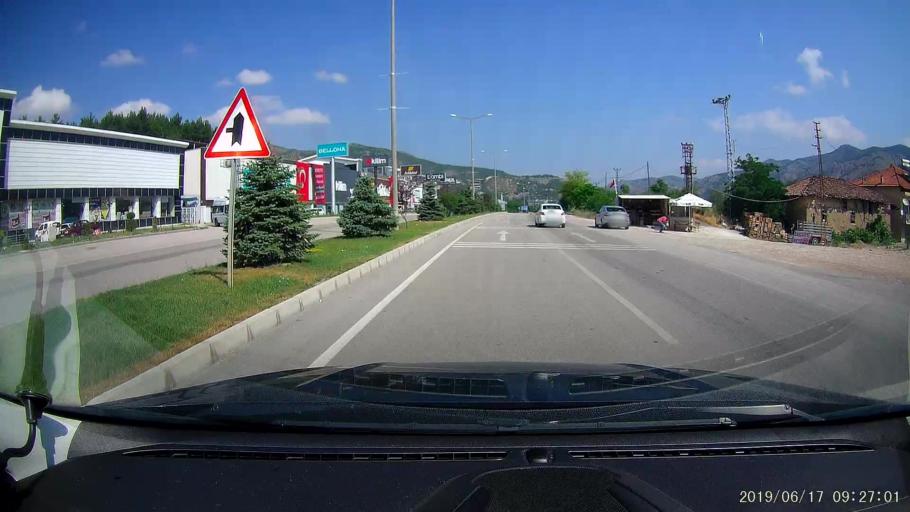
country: TR
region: Amasya
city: Amasya
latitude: 40.6730
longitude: 35.8299
